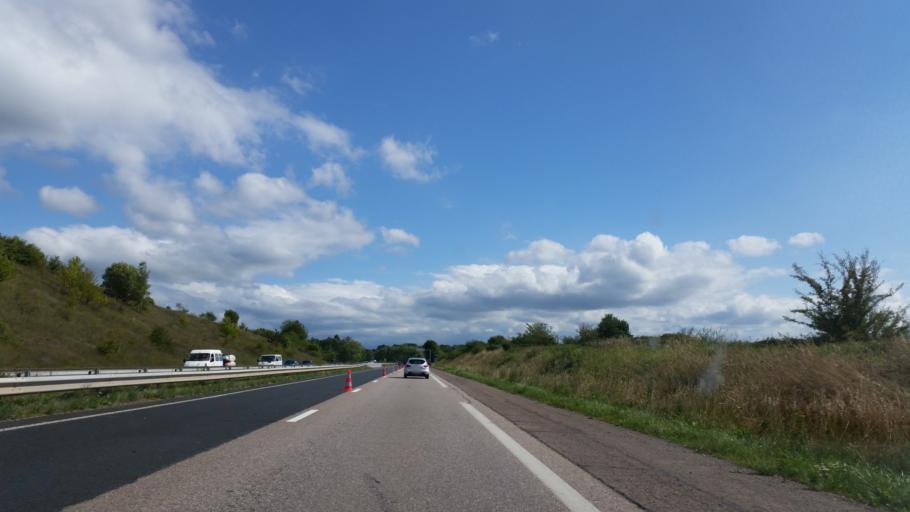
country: FR
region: Lorraine
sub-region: Departement des Vosges
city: Dogneville
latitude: 48.2164
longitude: 6.4547
